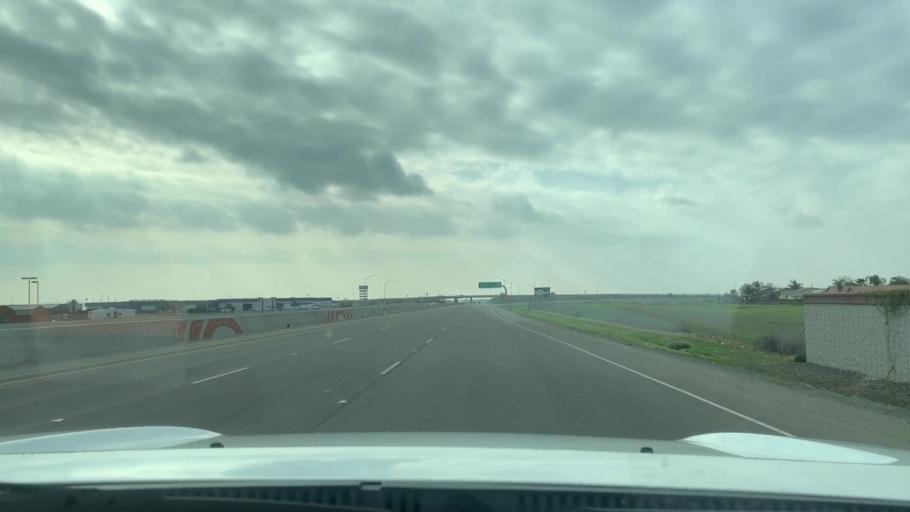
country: US
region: California
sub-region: Kings County
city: Lemoore
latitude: 36.2856
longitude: -119.8008
